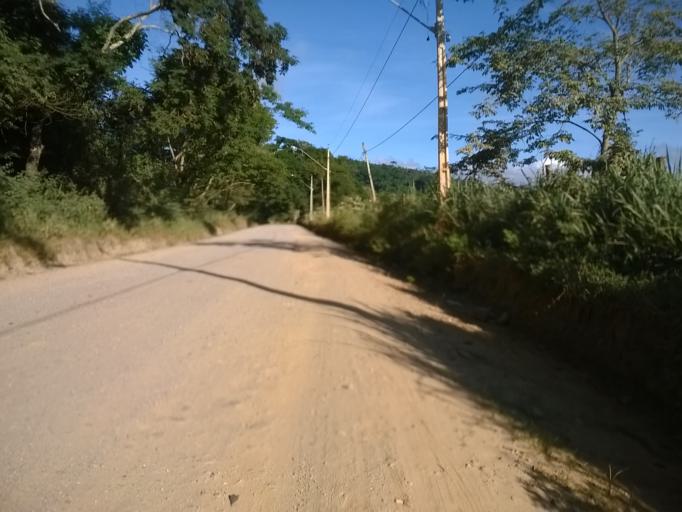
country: BR
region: Minas Gerais
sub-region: Uba
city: Uba
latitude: -21.0880
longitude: -42.9774
